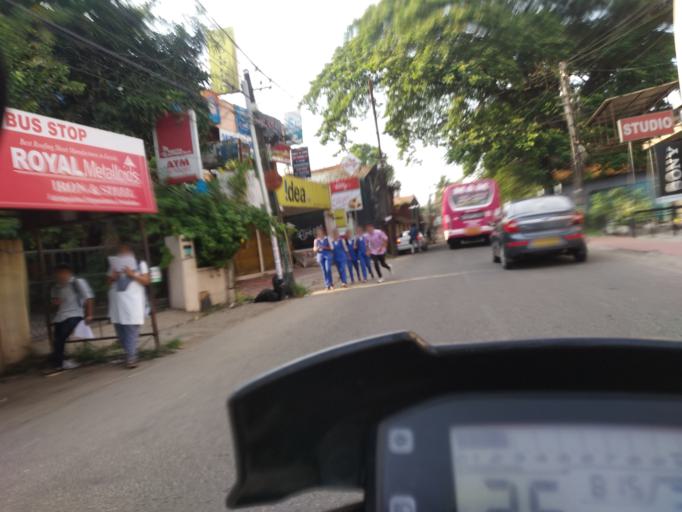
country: IN
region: Kerala
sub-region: Alappuzha
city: Arukutti
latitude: 9.9444
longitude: 76.3491
